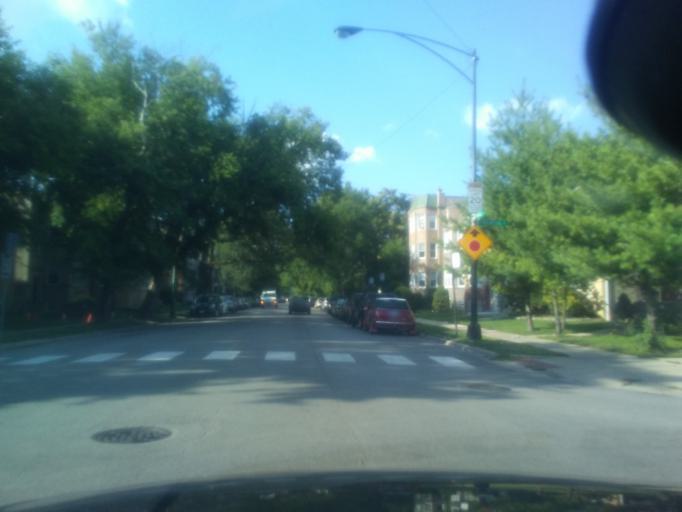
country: US
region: Illinois
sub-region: Cook County
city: Lincolnwood
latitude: 41.9794
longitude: -87.7136
